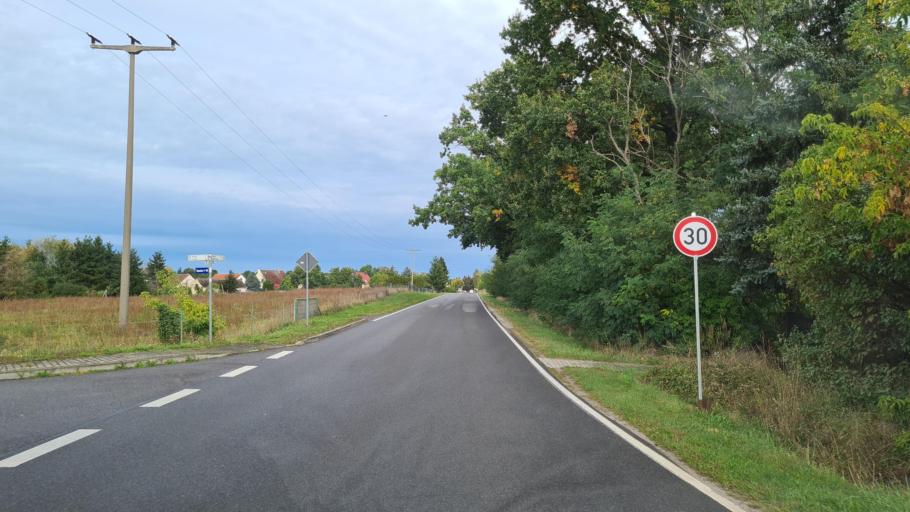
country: DE
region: Brandenburg
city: Luckau
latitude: 51.8674
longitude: 13.7298
